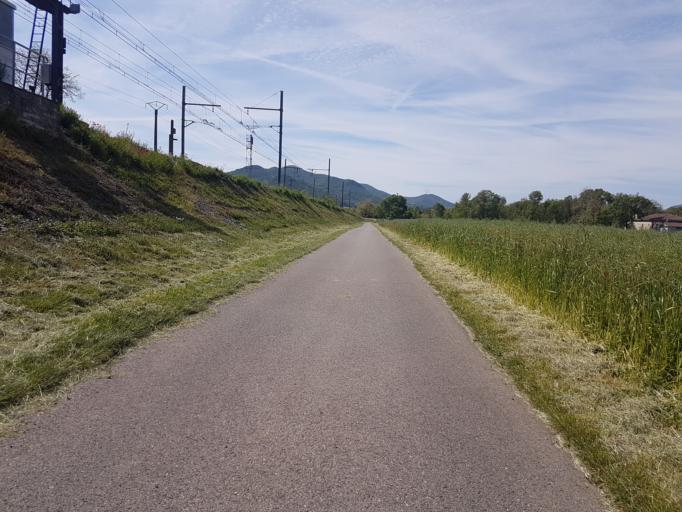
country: FR
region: Rhone-Alpes
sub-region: Departement de l'Ardeche
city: Le Pouzin
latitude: 44.7345
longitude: 4.7471
